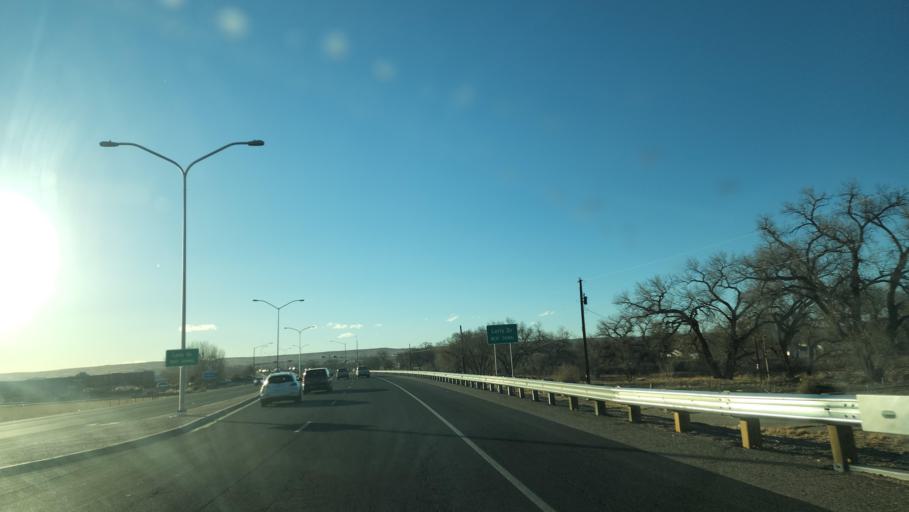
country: US
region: New Mexico
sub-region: Bernalillo County
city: South Valley
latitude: 35.0275
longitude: -106.7068
